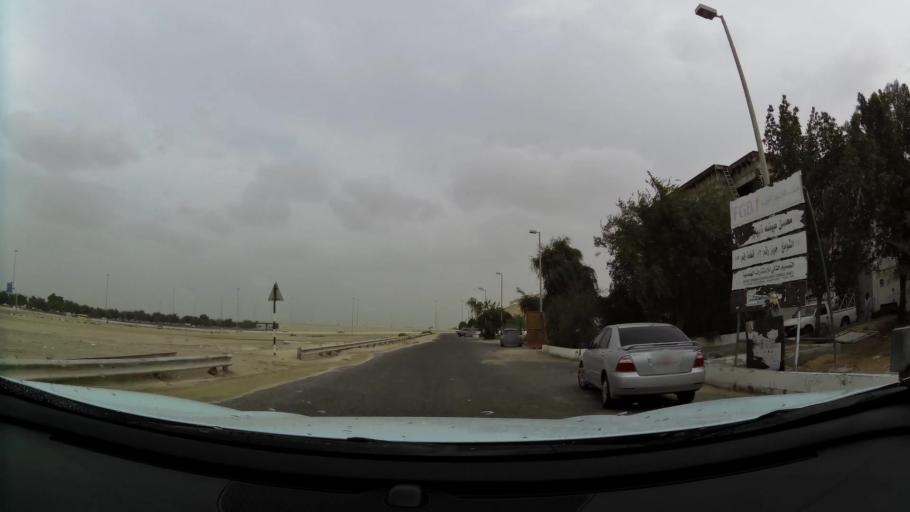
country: AE
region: Abu Dhabi
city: Abu Dhabi
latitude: 24.3640
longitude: 54.6545
